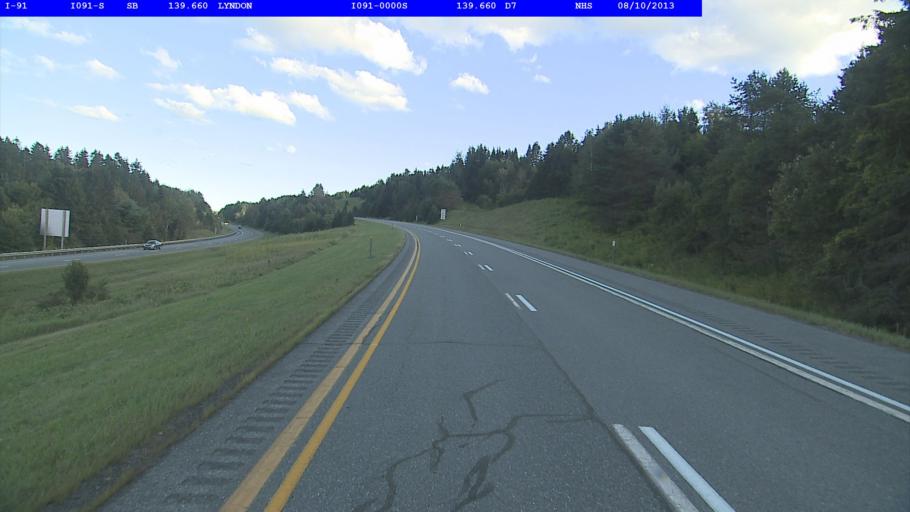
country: US
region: Vermont
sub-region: Caledonia County
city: Lyndonville
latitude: 44.5499
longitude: -72.0289
